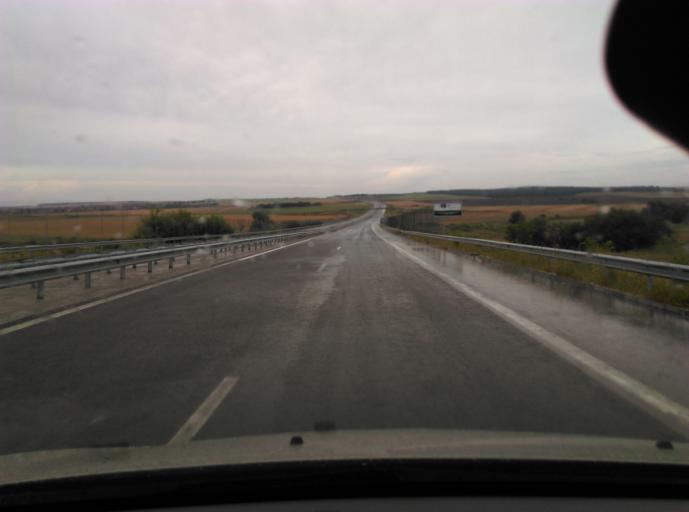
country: BG
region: Khaskovo
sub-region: Obshtina Dimitrovgrad
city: Dimitrovgrad
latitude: 42.0297
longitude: 25.5542
